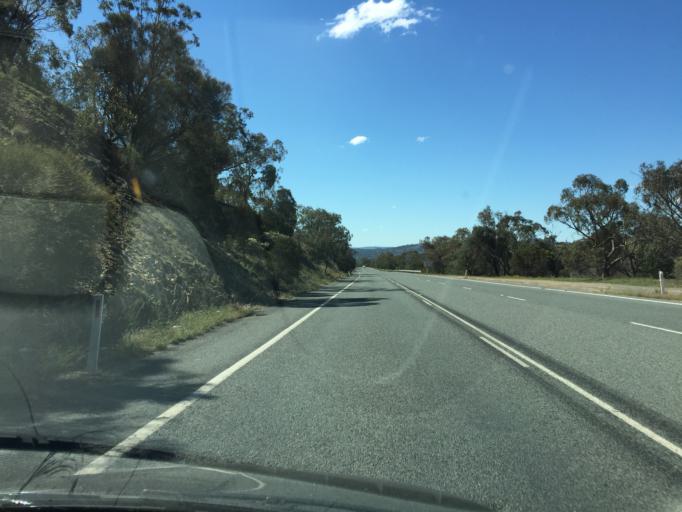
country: AU
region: Australian Capital Territory
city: Macarthur
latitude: -35.4641
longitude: 149.1348
